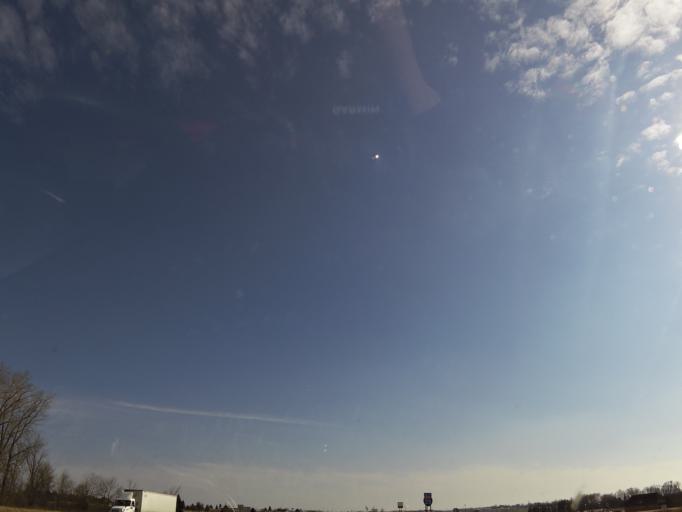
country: US
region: Minnesota
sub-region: Steele County
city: Medford
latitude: 44.1331
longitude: -93.2481
